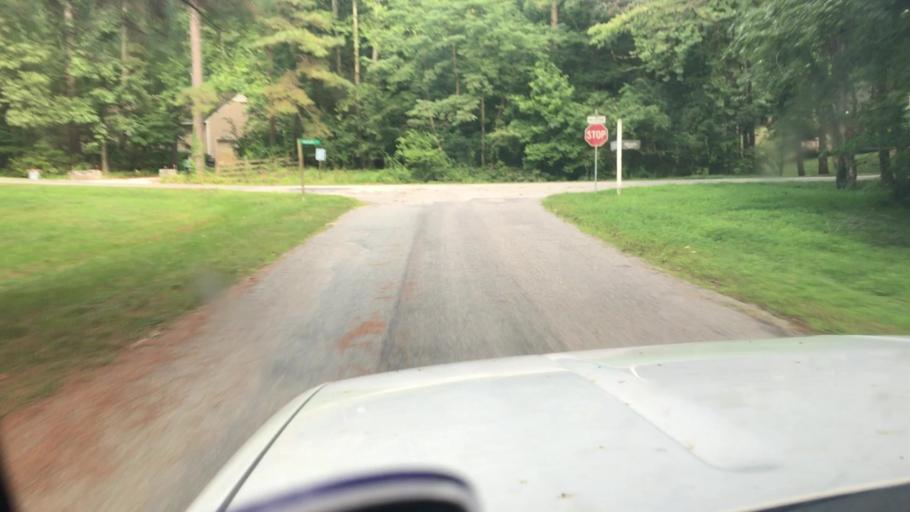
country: US
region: Virginia
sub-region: Henrico County
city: Short Pump
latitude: 37.6065
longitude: -77.7132
